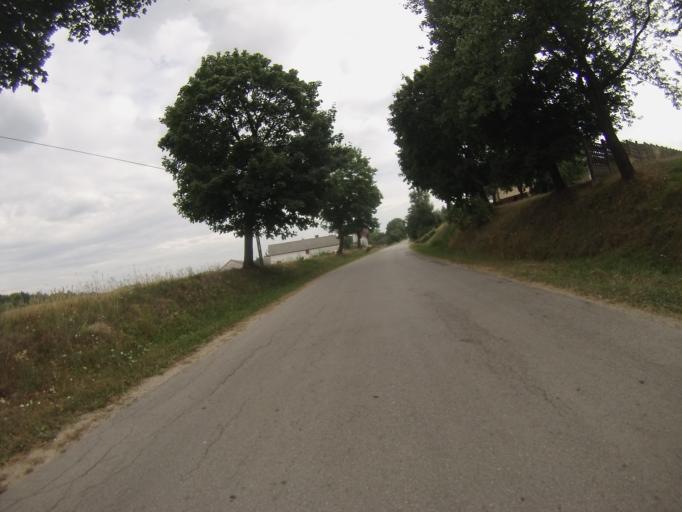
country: PL
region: Swietokrzyskie
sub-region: Powiat kielecki
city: Lagow
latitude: 50.7210
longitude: 21.1146
